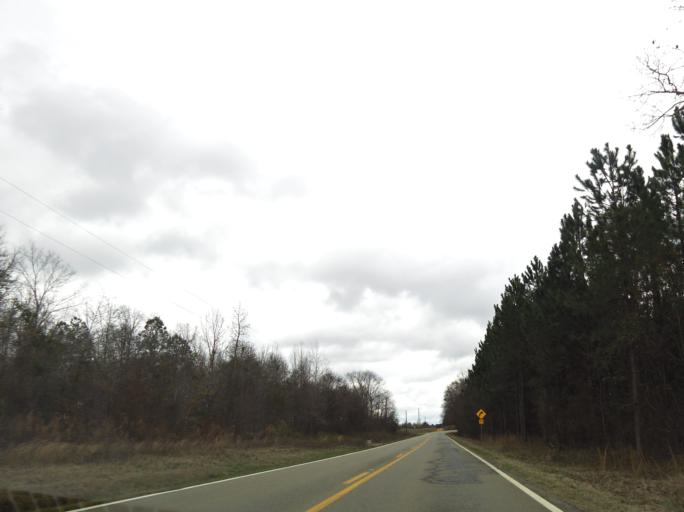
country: US
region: Georgia
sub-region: Bleckley County
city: Cochran
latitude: 32.5325
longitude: -83.3677
